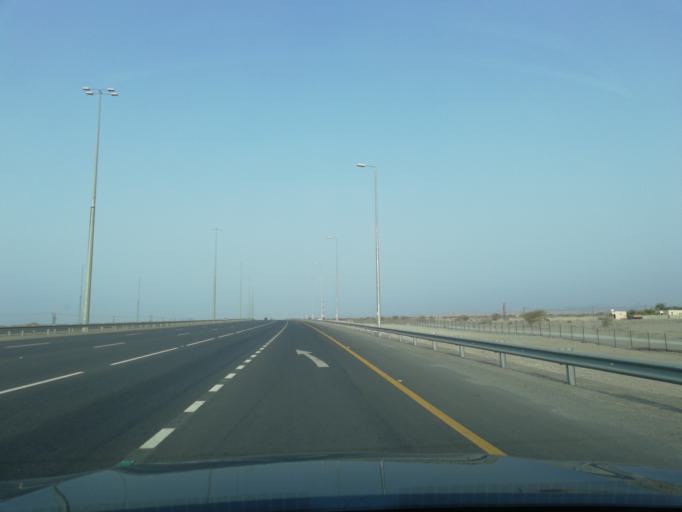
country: OM
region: Al Batinah
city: Barka'
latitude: 23.6187
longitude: 57.9111
